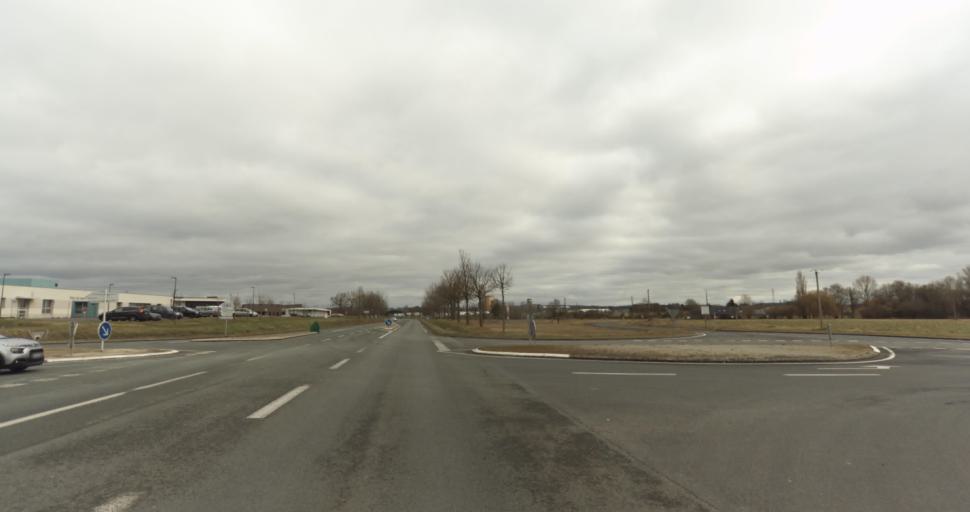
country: FR
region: Pays de la Loire
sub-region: Departement de Maine-et-Loire
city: Jumelles
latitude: 47.3702
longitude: -0.1057
